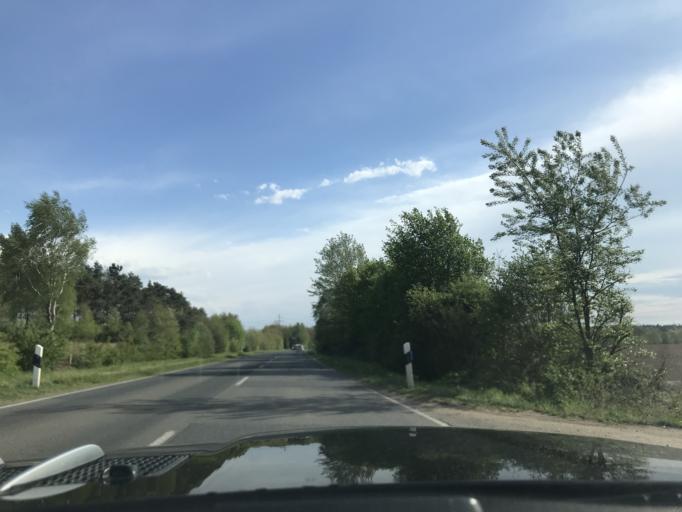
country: DE
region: Schleswig-Holstein
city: Siebeneichen
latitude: 53.5050
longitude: 10.6137
